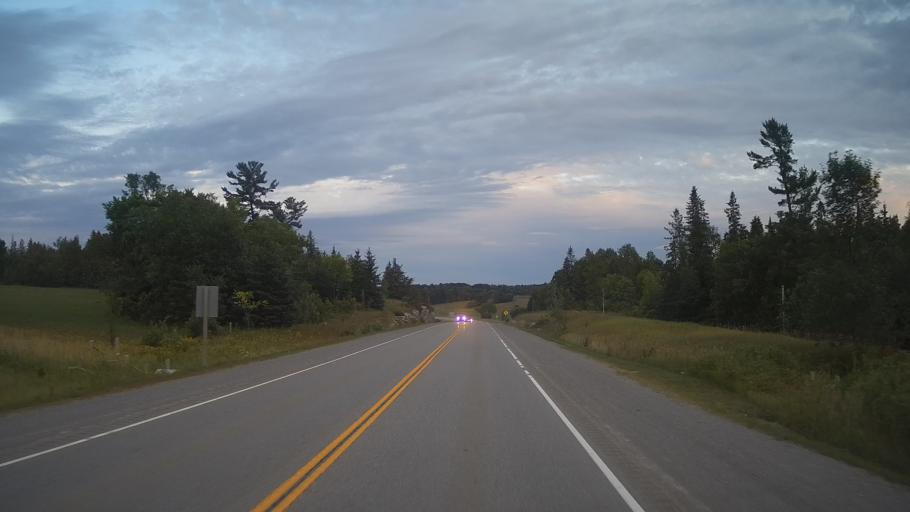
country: CA
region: Ontario
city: Pembroke
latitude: 45.7307
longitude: -76.9976
